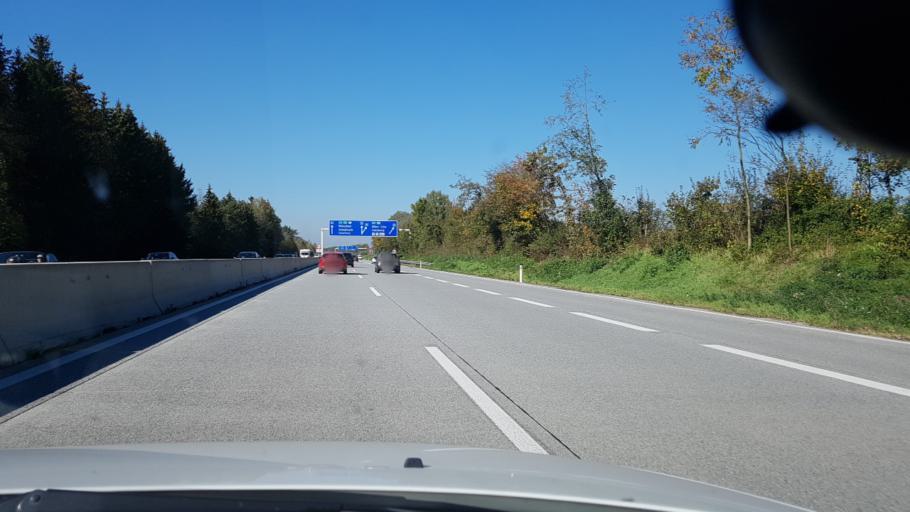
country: AT
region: Salzburg
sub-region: Politischer Bezirk Salzburg-Umgebung
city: Grodig
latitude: 47.7572
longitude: 13.0065
